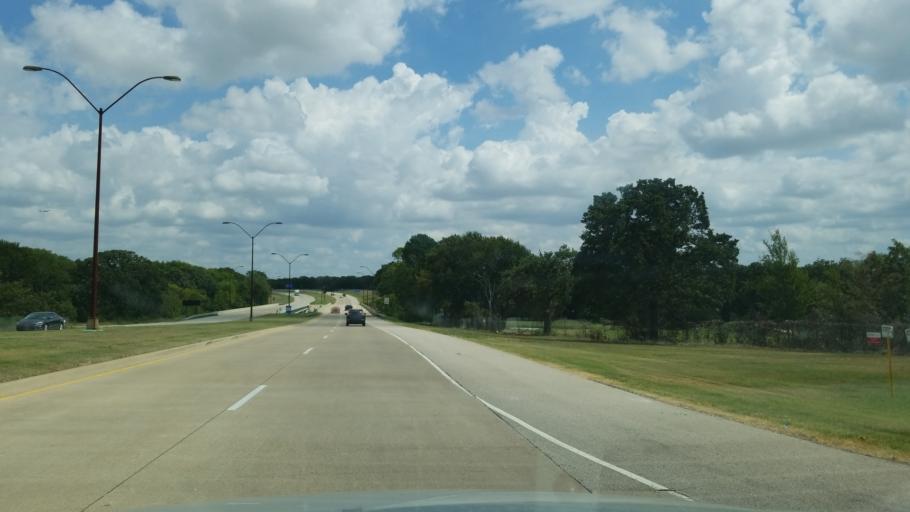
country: US
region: Texas
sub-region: Tarrant County
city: Euless
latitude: 32.8671
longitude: -97.0629
